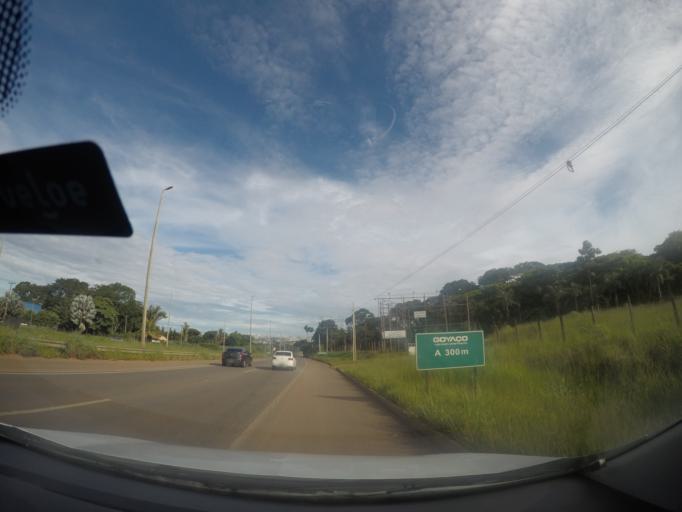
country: BR
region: Goias
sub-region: Goiania
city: Goiania
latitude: -16.6288
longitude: -49.3510
